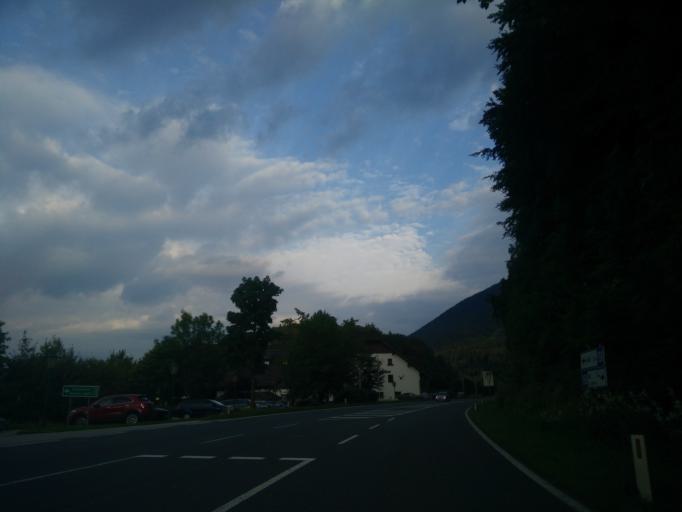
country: AT
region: Salzburg
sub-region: Politischer Bezirk Salzburg-Umgebung
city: Thalgau
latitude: 47.8113
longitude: 13.2456
